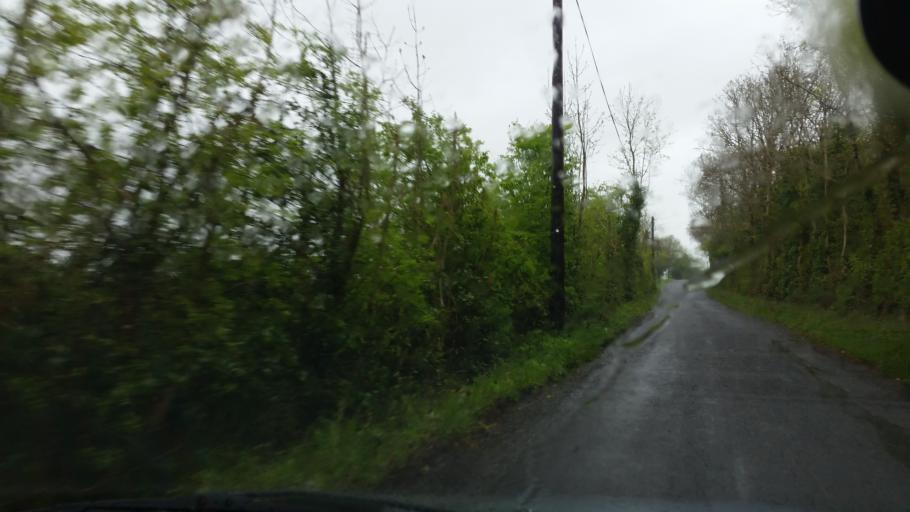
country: GB
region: Northern Ireland
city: Fivemiletown
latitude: 54.3047
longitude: -7.2939
